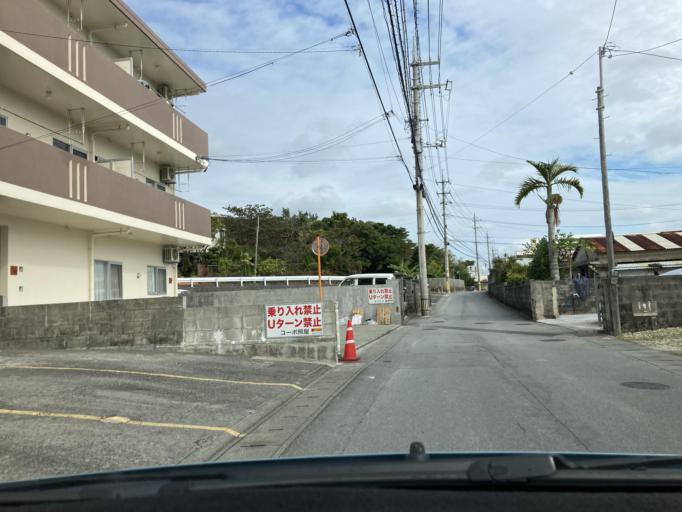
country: JP
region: Okinawa
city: Ginowan
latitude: 26.2047
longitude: 127.7530
